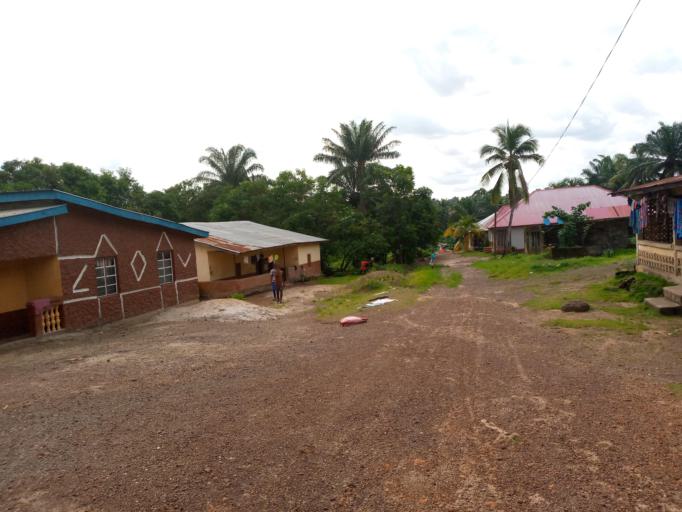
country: SL
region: Northern Province
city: Magburaka
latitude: 8.7251
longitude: -11.9438
